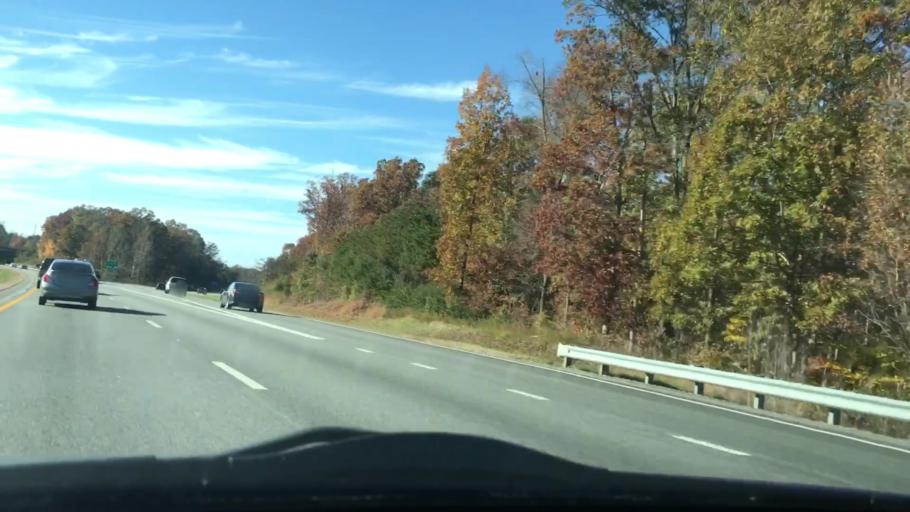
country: US
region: North Carolina
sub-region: Guilford County
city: High Point
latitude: 36.0087
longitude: -80.0055
